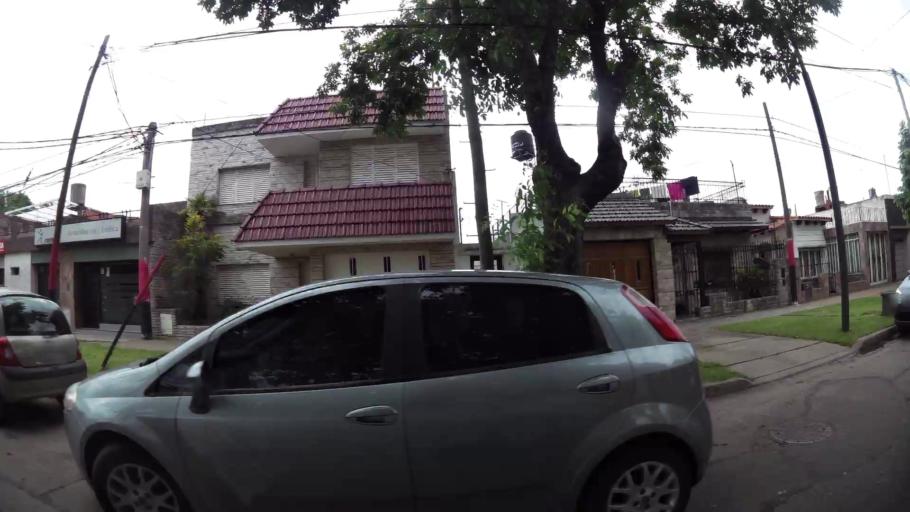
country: AR
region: Santa Fe
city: Gobernador Galvez
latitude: -33.0000
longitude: -60.6530
